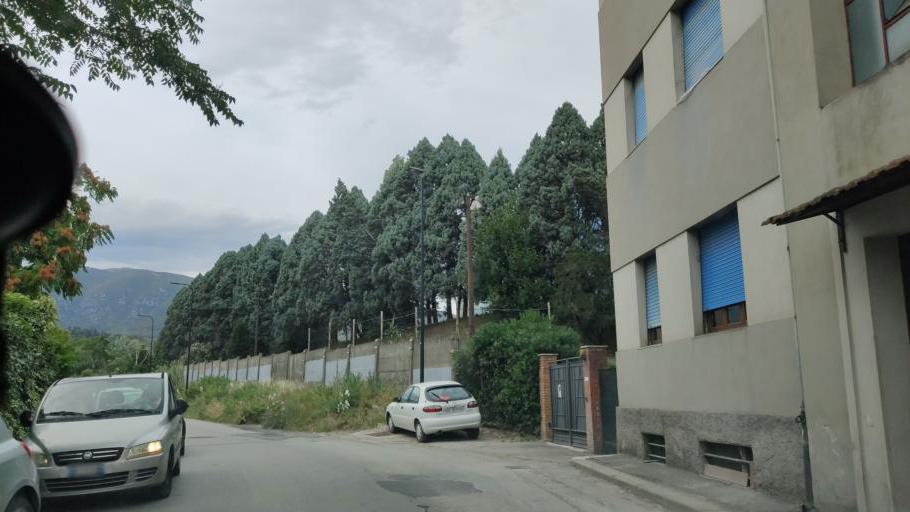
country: IT
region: Umbria
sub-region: Provincia di Terni
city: Terni
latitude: 42.5646
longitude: 12.6590
